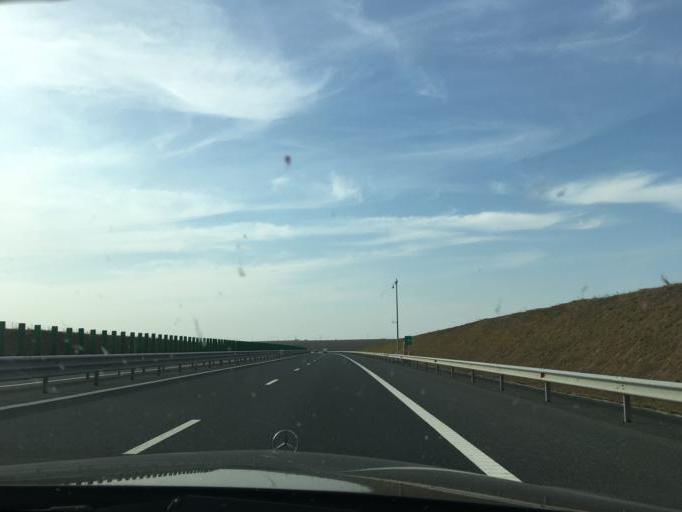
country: RO
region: Constanta
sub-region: Municipiul Medgidia
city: Valea Dacilor
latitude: 44.2032
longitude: 28.2763
